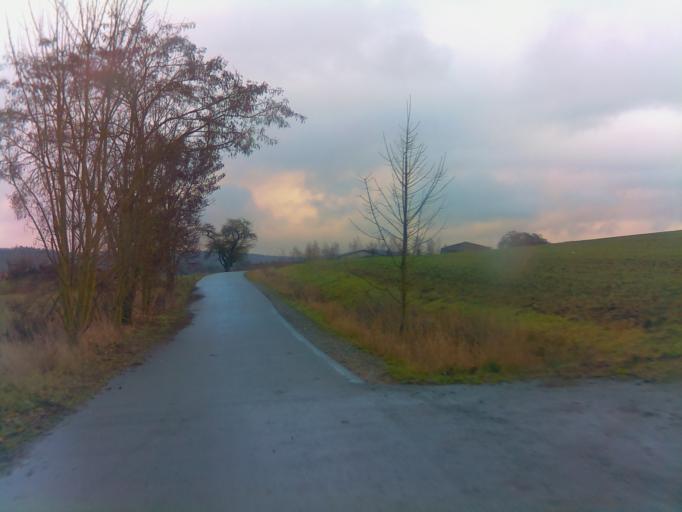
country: DE
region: Thuringia
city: Wolfershausen
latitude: 50.4719
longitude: 10.4261
